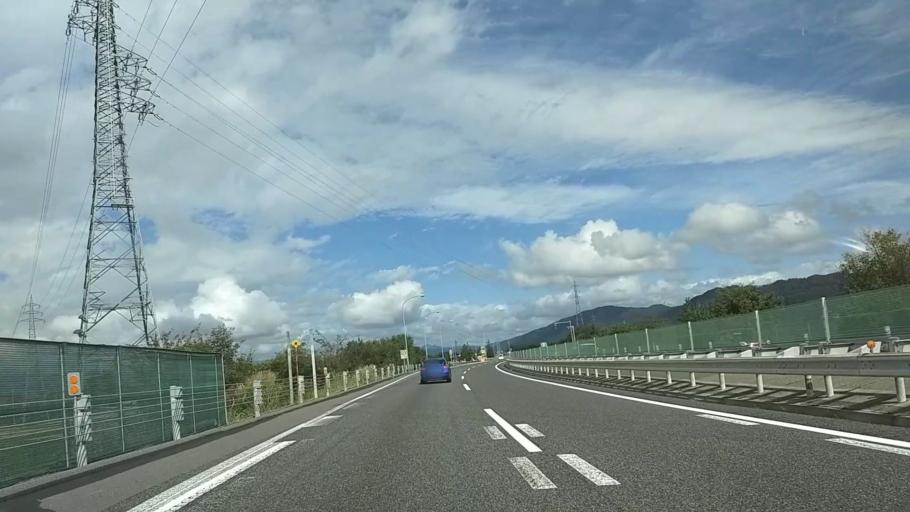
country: JP
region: Nagano
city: Matsumoto
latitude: 36.2565
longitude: 137.9350
